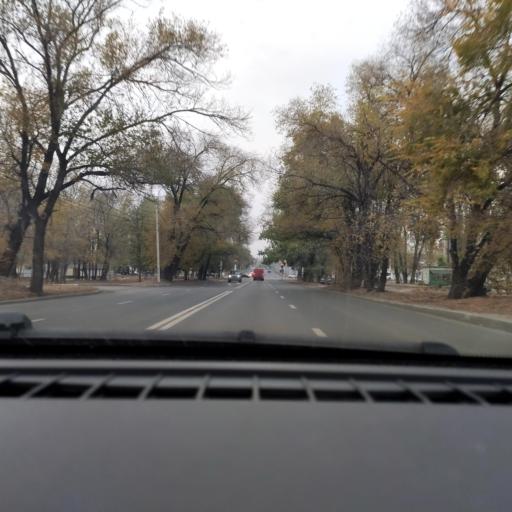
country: RU
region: Voronezj
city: Maslovka
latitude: 51.5986
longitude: 39.2437
